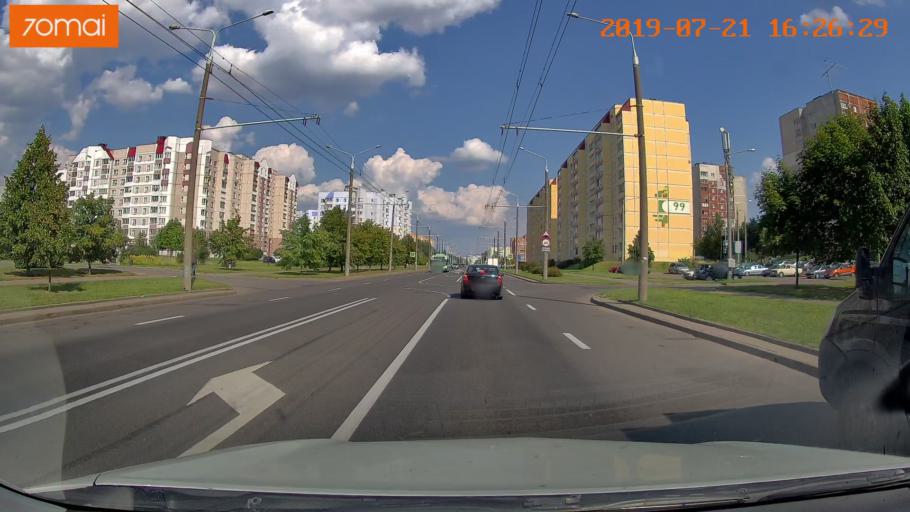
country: BY
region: Minsk
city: Novoye Medvezhino
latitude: 53.9011
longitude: 27.4297
